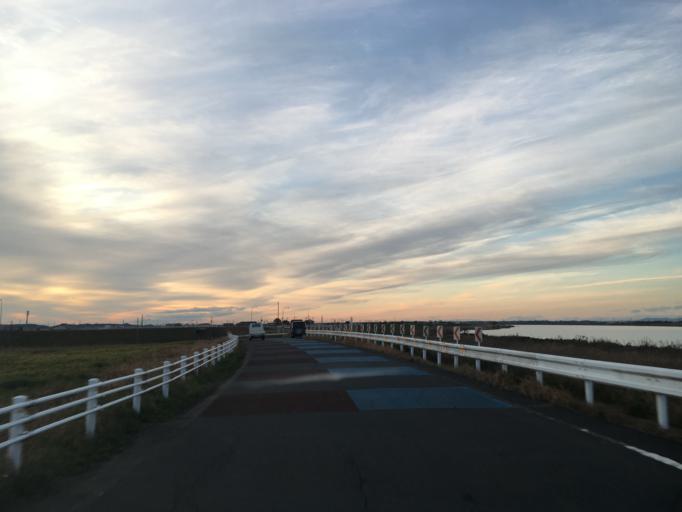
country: JP
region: Chiba
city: Katori-shi
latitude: 35.9066
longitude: 140.4878
